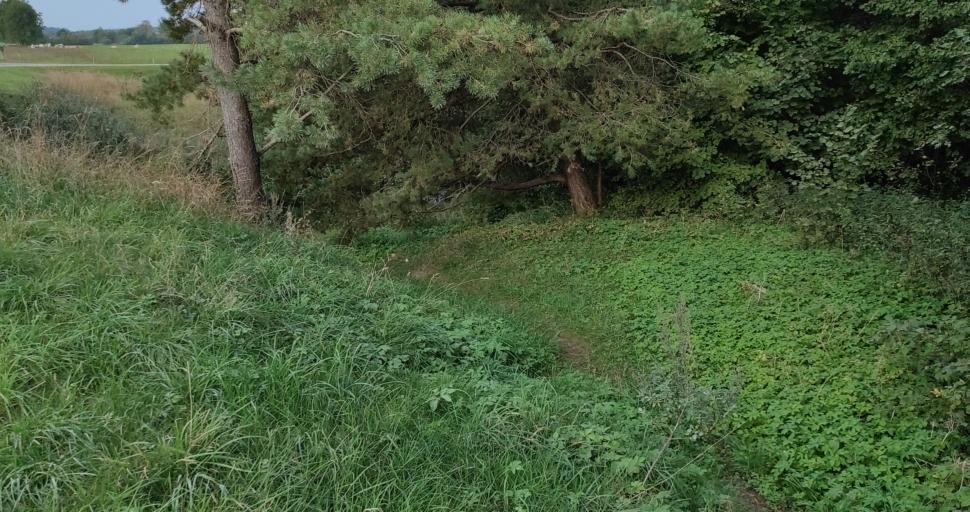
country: LV
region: Kuldigas Rajons
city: Kuldiga
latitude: 57.2206
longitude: 22.0935
